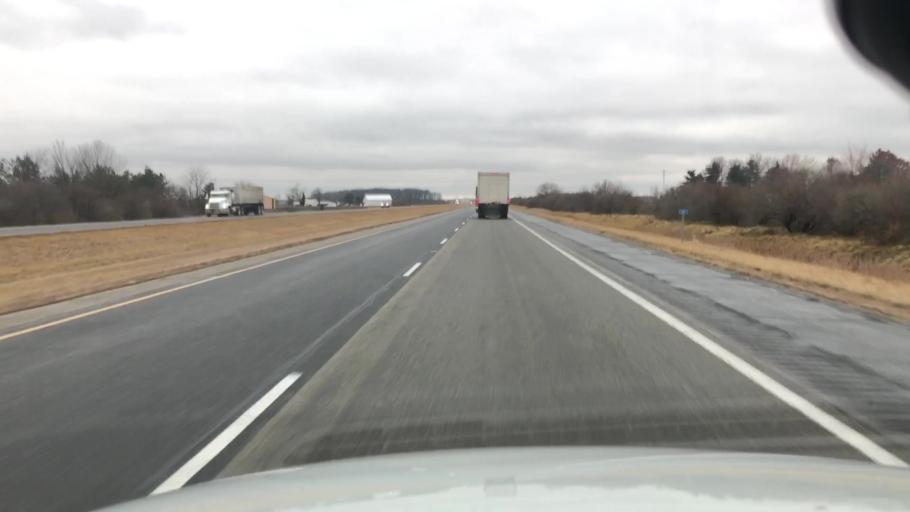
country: US
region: Indiana
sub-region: Allen County
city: Monroeville
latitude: 41.0049
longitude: -84.8373
